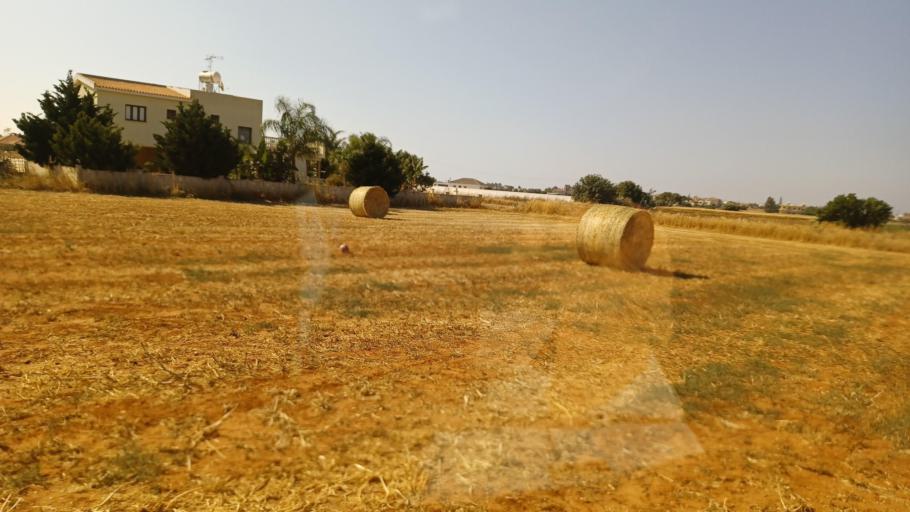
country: CY
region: Ammochostos
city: Frenaros
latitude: 35.0380
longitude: 33.9422
